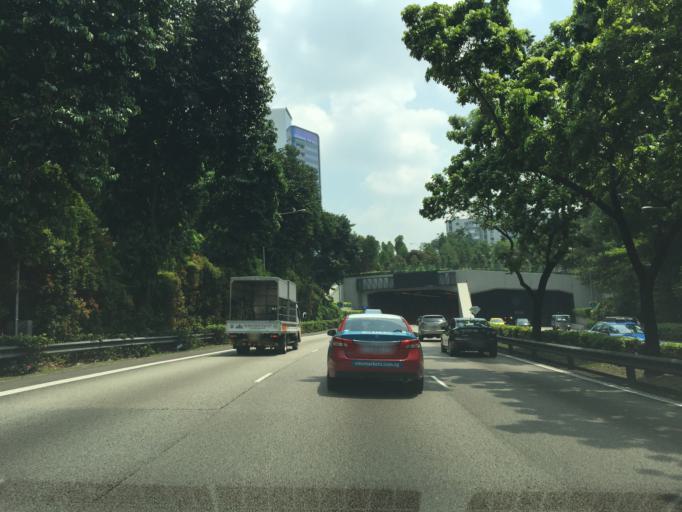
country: SG
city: Singapore
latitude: 1.3051
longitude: 103.8399
